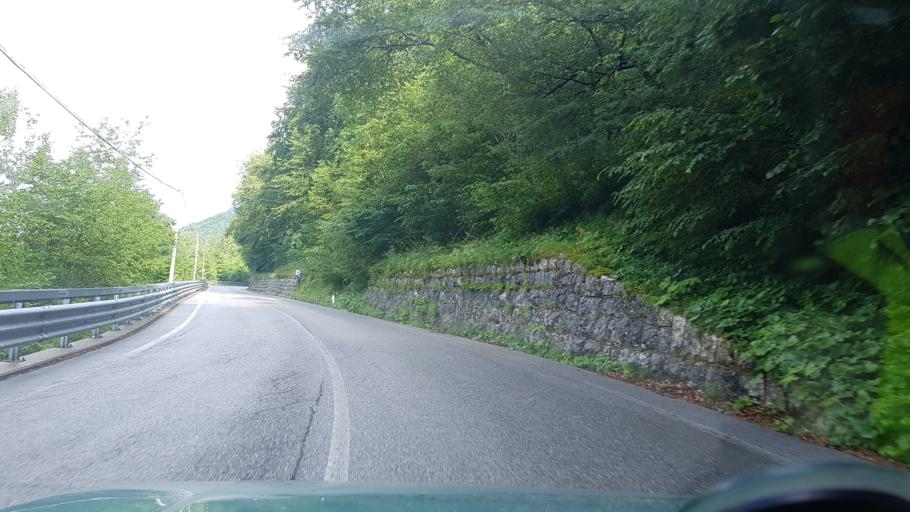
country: IT
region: Friuli Venezia Giulia
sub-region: Provincia di Udine
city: Lusevera
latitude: 46.3060
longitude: 13.2857
